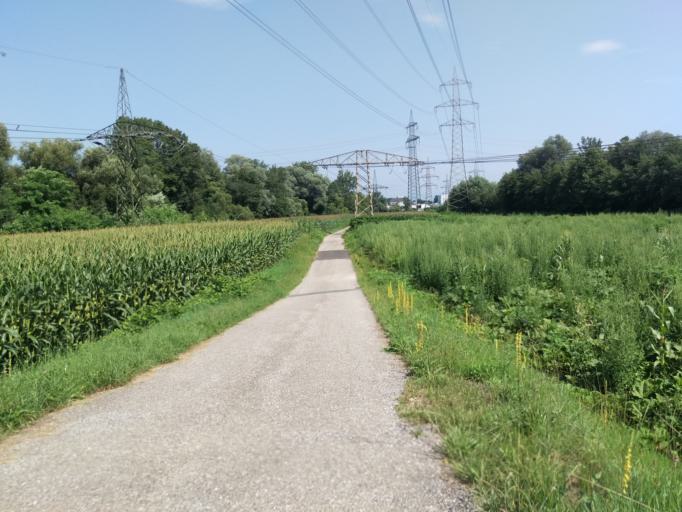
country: AT
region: Styria
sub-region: Politischer Bezirk Graz-Umgebung
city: Werndorf
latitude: 46.9106
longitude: 15.4836
